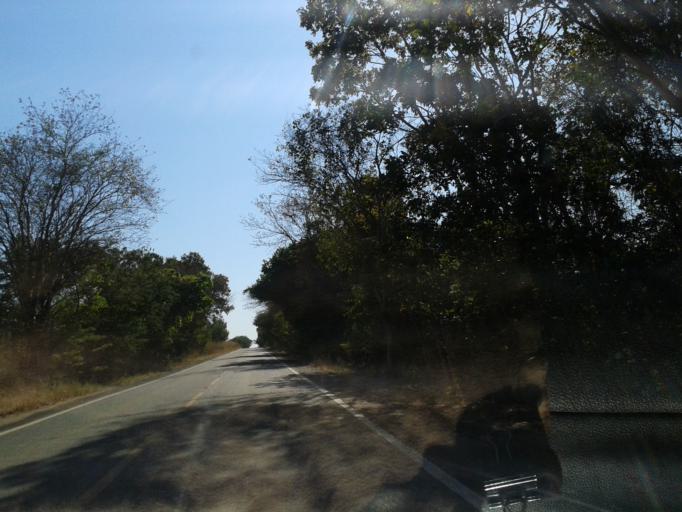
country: BR
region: Goias
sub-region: Mozarlandia
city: Mozarlandia
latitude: -14.4838
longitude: -50.4781
